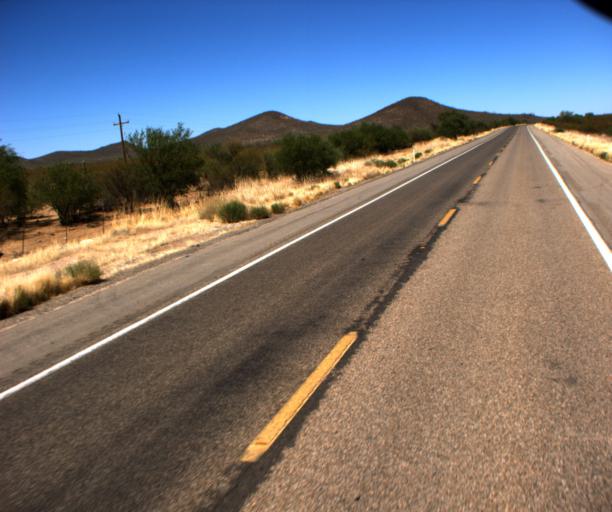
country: US
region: Arizona
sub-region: Pima County
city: Three Points
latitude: 32.0588
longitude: -111.3991
